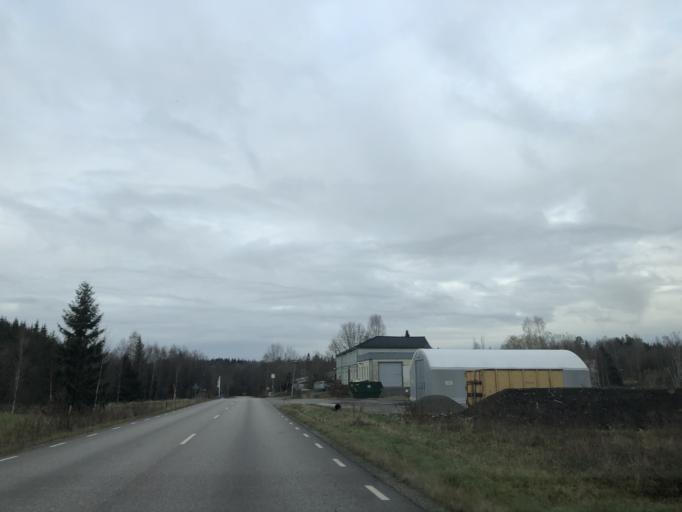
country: SE
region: Vaestra Goetaland
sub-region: Ulricehamns Kommun
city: Ulricehamn
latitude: 57.6755
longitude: 13.4010
